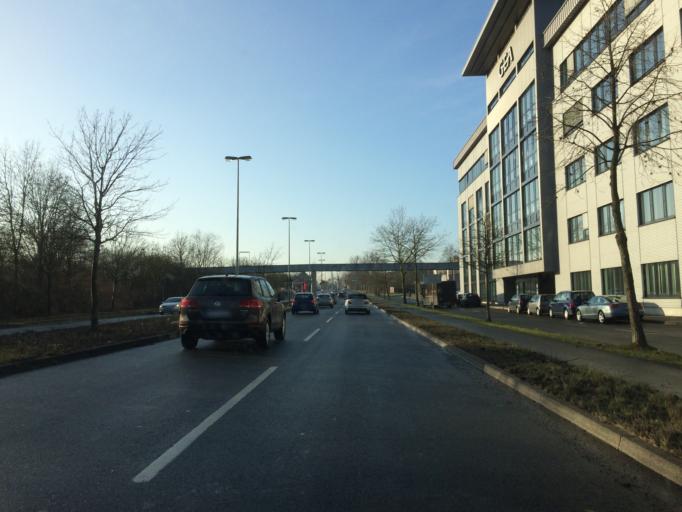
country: DE
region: North Rhine-Westphalia
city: Bochum-Hordel
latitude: 51.5141
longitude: 7.1904
